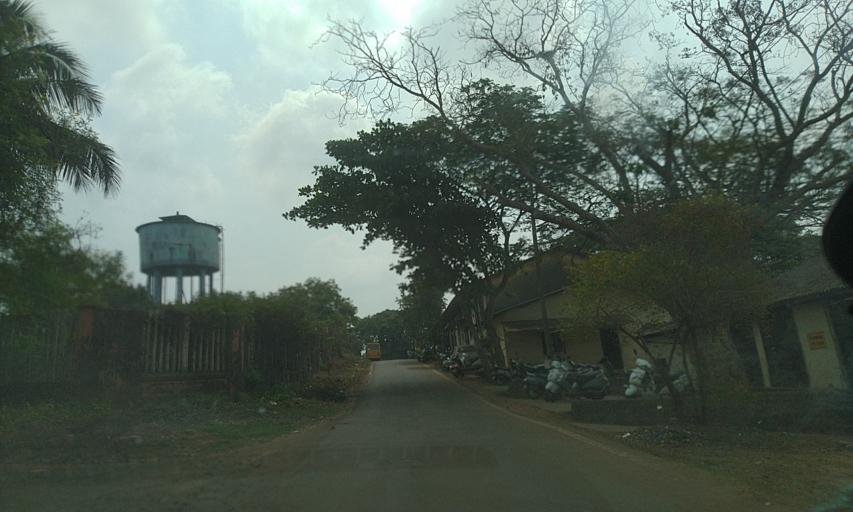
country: IN
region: Goa
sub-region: North Goa
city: Panaji
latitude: 15.4875
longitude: 73.8287
